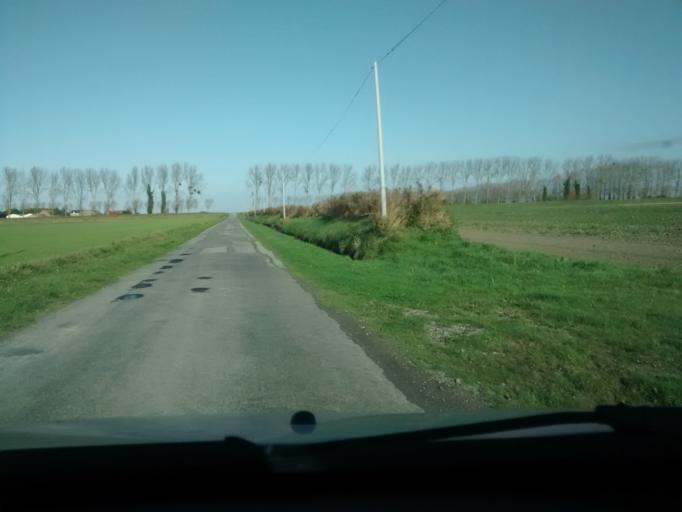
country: FR
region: Brittany
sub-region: Departement d'Ille-et-Vilaine
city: Roz-sur-Couesnon
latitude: 48.6116
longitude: -1.5817
